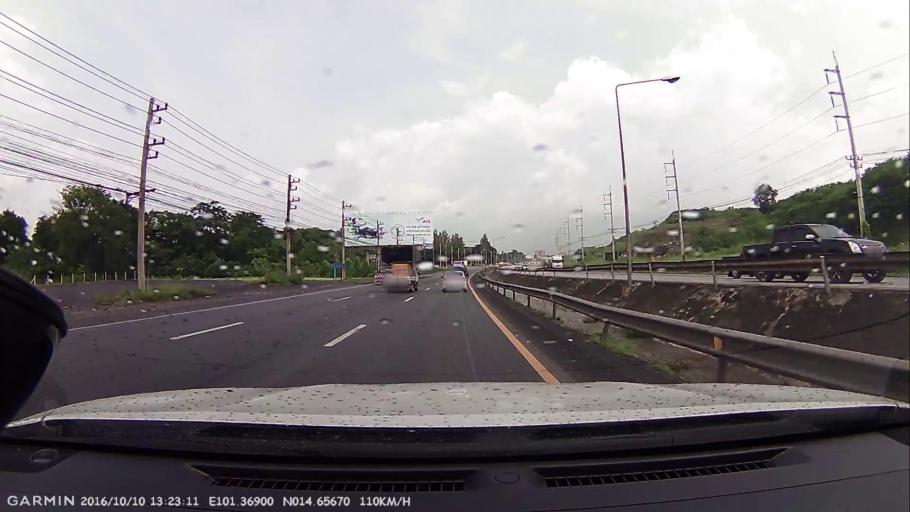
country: TH
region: Nakhon Ratchasima
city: Pak Chong
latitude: 14.6567
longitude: 101.3689
